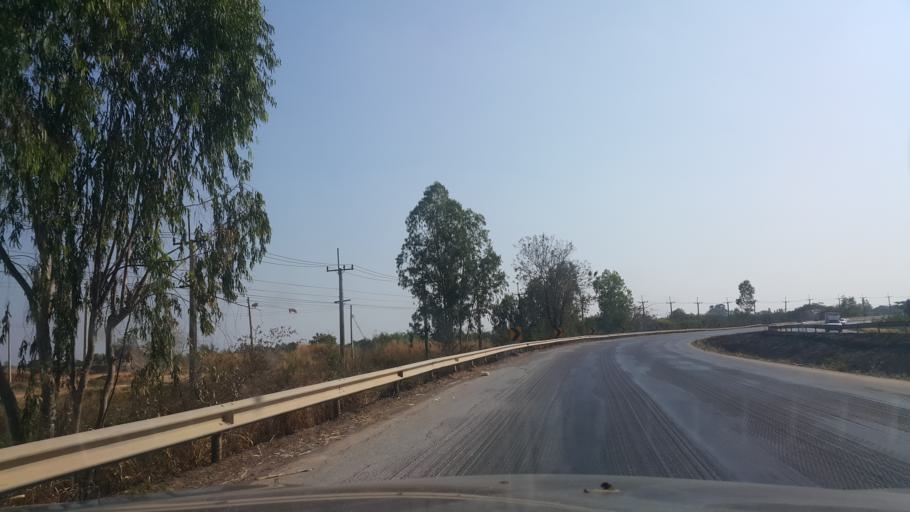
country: TH
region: Khon Kaen
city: Khon Kaen
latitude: 16.4217
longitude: 102.9171
